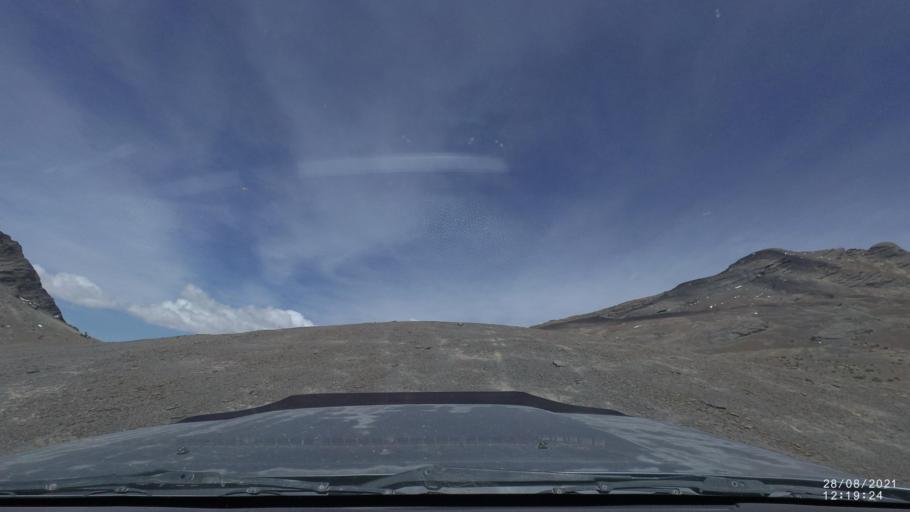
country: BO
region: Cochabamba
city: Sipe Sipe
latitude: -17.2806
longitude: -66.3828
